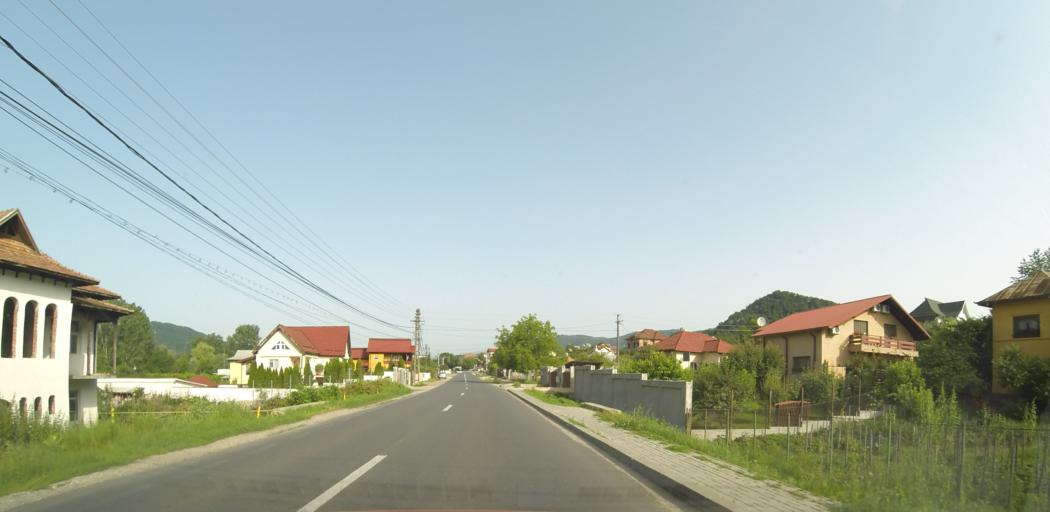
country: RO
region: Valcea
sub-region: Comuna Vladesti
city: Vladesti
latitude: 45.1163
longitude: 24.3165
